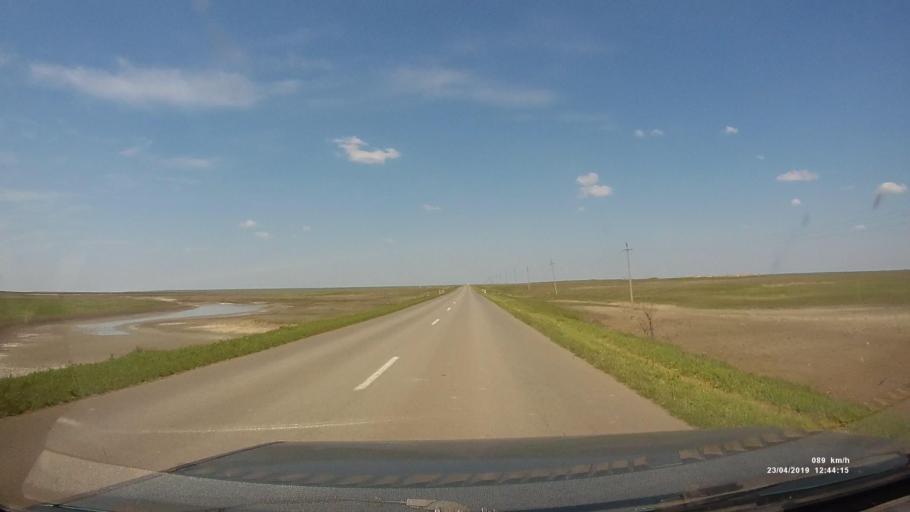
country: RU
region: Kalmykiya
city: Yashalta
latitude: 46.4744
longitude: 42.6484
